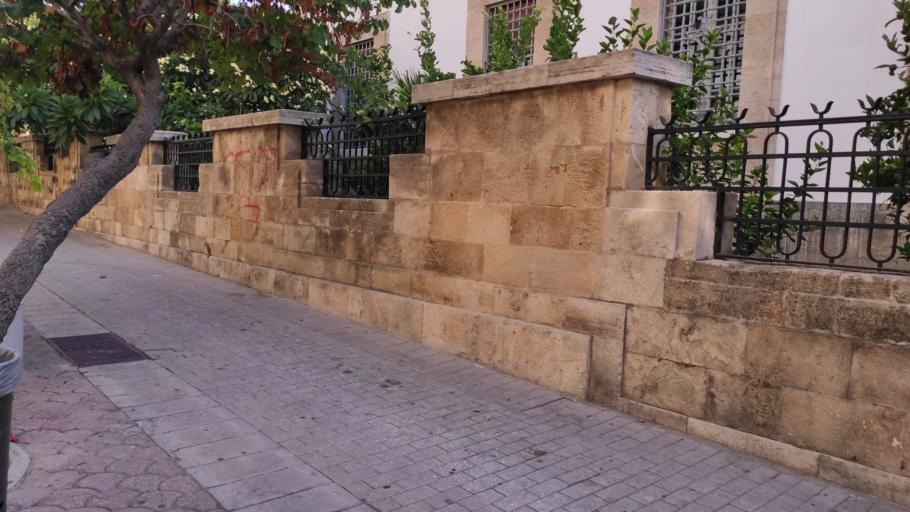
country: GR
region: South Aegean
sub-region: Nomos Dodekanisou
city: Rodos
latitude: 36.4483
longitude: 28.2249
